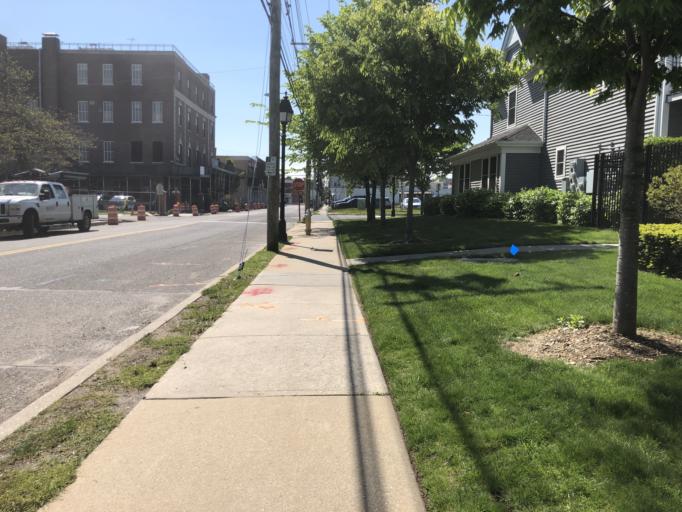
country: US
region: New York
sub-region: Suffolk County
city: Bay Shore
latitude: 40.7227
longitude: -73.2494
